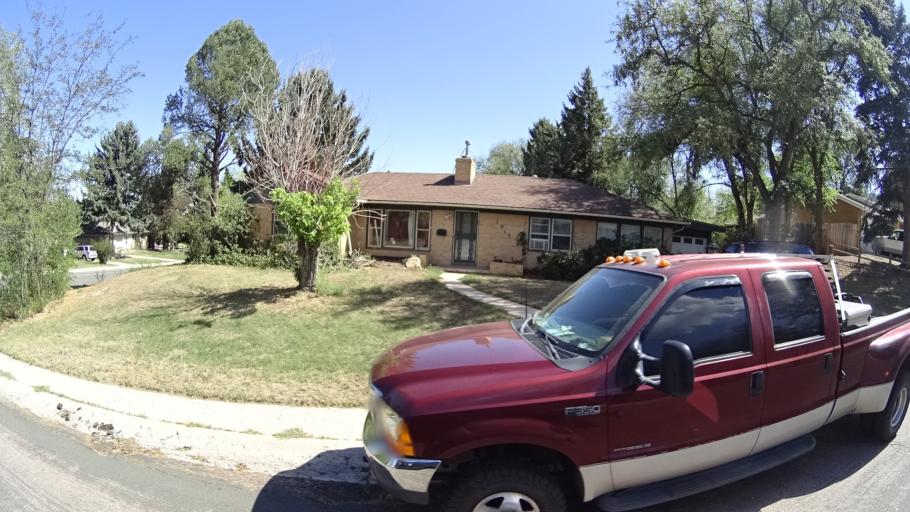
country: US
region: Colorado
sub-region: El Paso County
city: Colorado Springs
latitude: 38.8100
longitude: -104.8484
